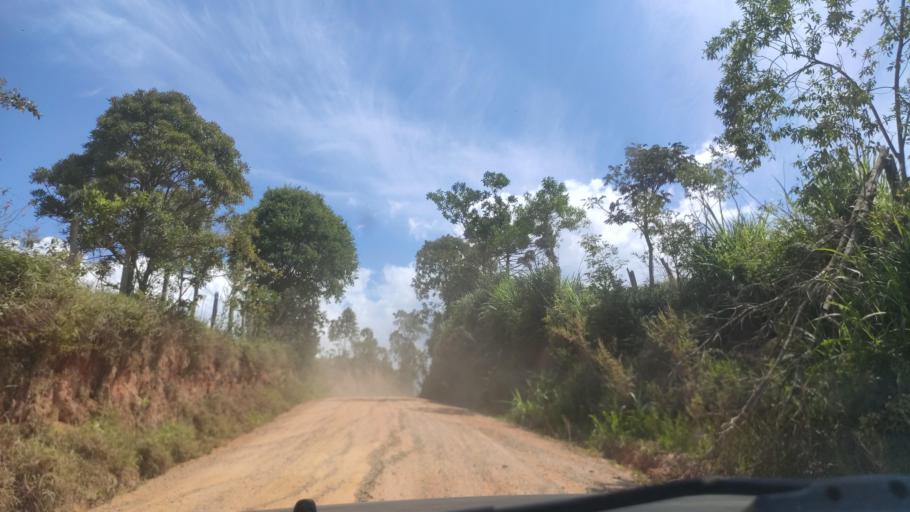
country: BR
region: Minas Gerais
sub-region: Cambui
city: Cambui
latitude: -22.7149
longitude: -46.0377
